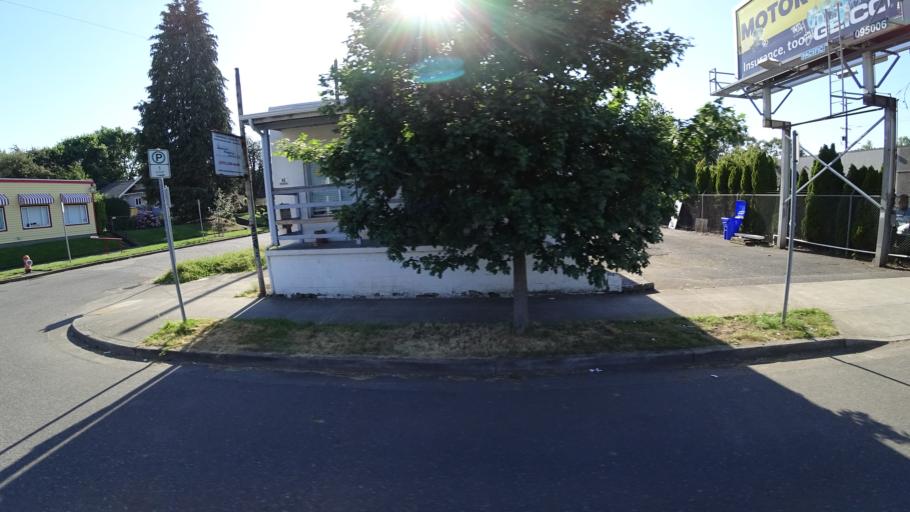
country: US
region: Oregon
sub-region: Multnomah County
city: Portland
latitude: 45.5657
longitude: -122.6823
